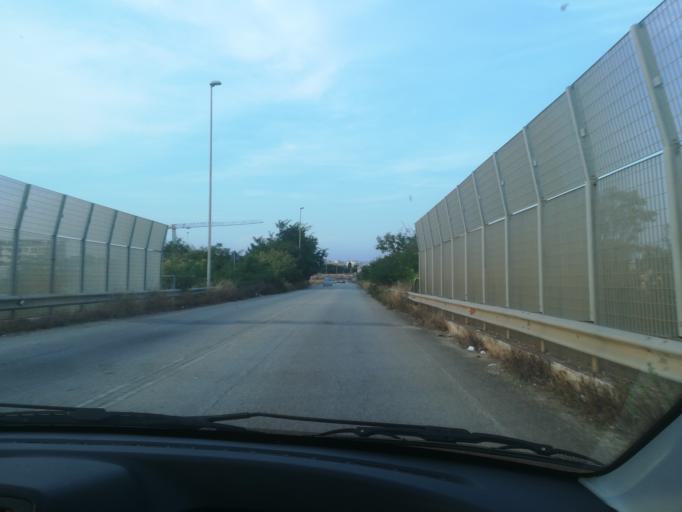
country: IT
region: Apulia
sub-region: Provincia di Bari
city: Monopoli
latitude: 40.9356
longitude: 17.2924
